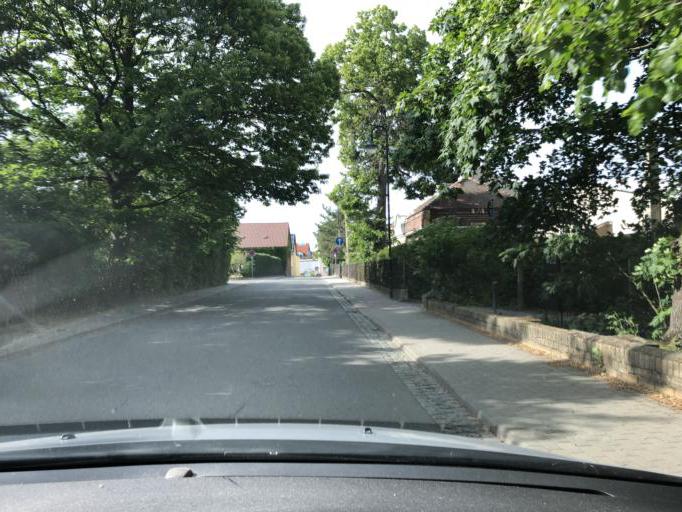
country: DE
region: Saxony
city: Brandis
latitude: 51.3305
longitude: 12.6051
